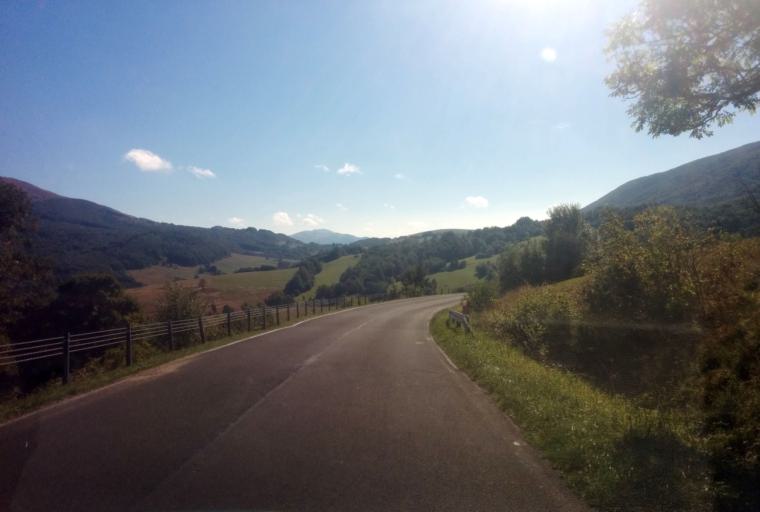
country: PL
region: Subcarpathian Voivodeship
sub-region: Powiat bieszczadzki
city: Lutowiska
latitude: 49.1406
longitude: 22.5522
